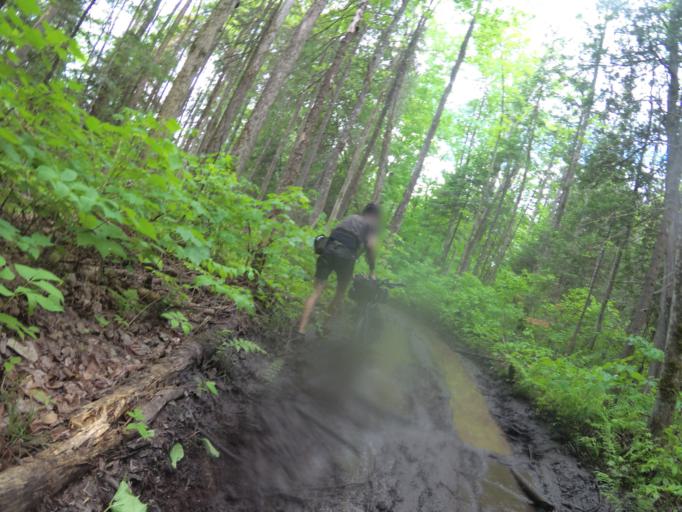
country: CA
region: Ontario
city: Renfrew
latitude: 45.1296
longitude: -76.8341
